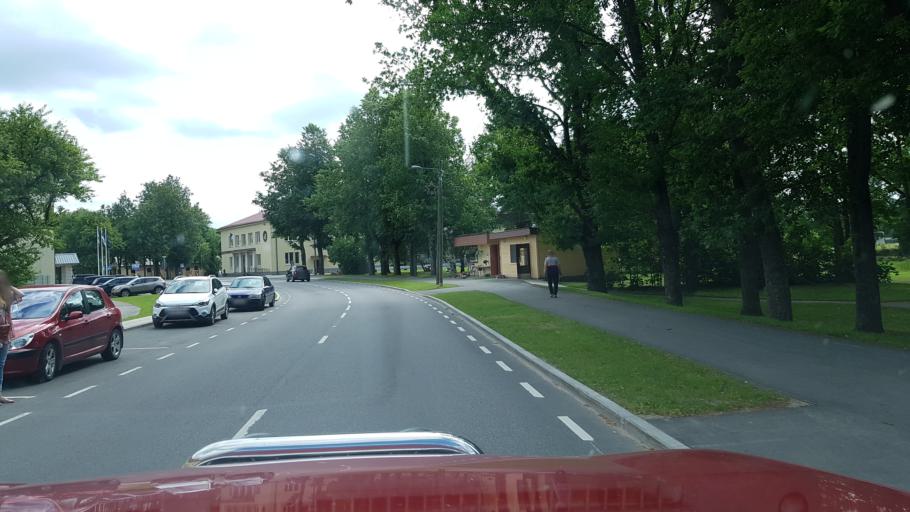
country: EE
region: Jogevamaa
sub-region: Mustvee linn
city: Mustvee
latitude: 58.8478
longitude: 26.9417
